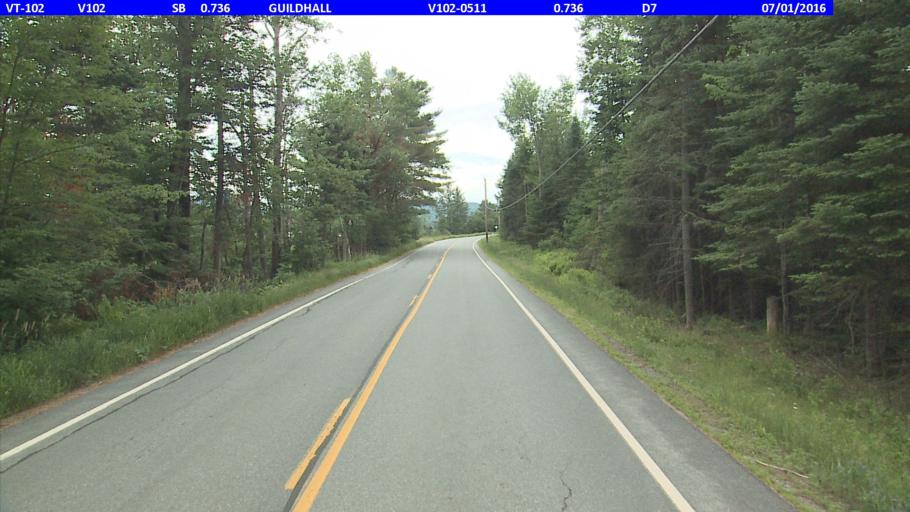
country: US
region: New Hampshire
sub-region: Coos County
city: Lancaster
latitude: 44.5060
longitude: -71.5939
